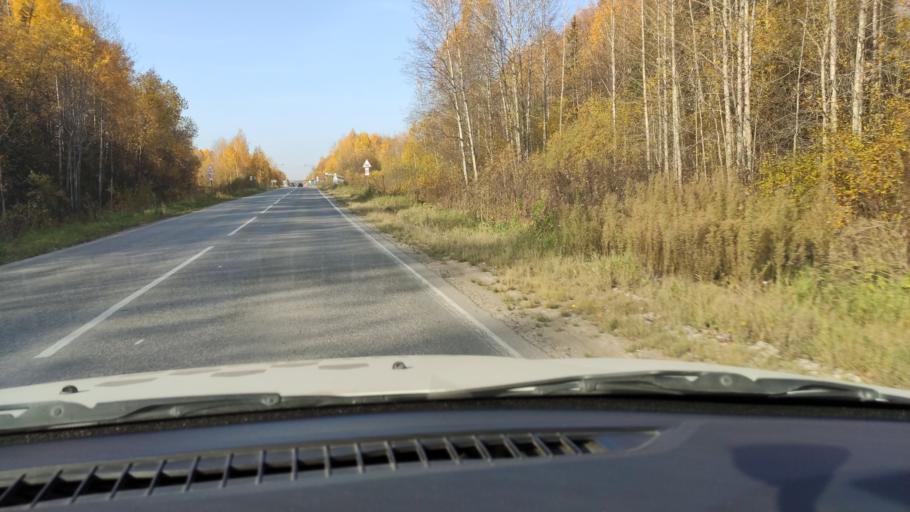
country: RU
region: Perm
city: Novyye Lyady
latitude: 58.0277
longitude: 56.6279
